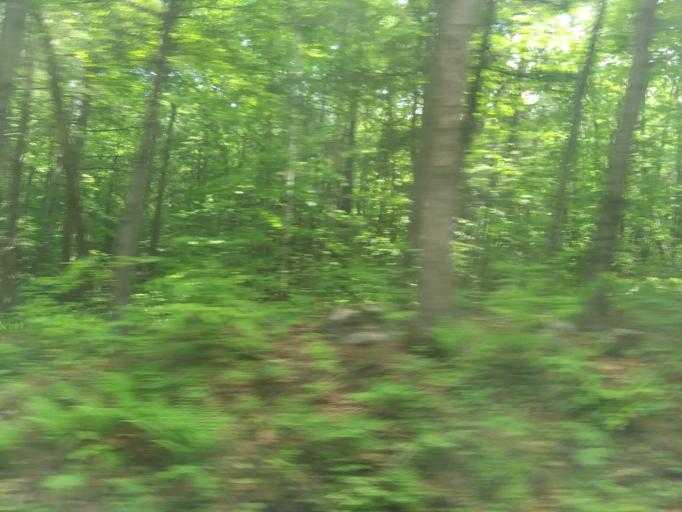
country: US
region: Massachusetts
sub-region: Franklin County
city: Shelburne Falls
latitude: 42.5819
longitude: -72.7514
